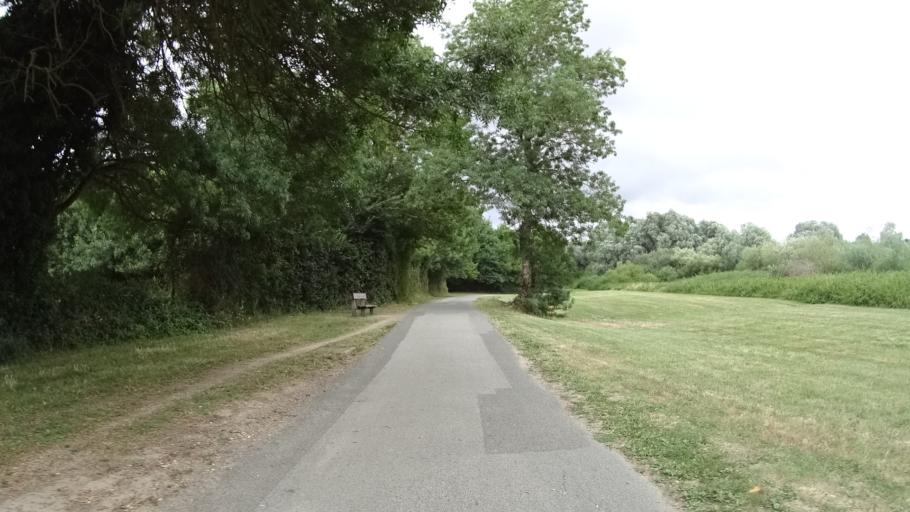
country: FR
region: Pays de la Loire
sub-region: Departement de la Loire-Atlantique
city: Thouare-sur-Loire
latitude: 47.2581
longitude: -1.4414
